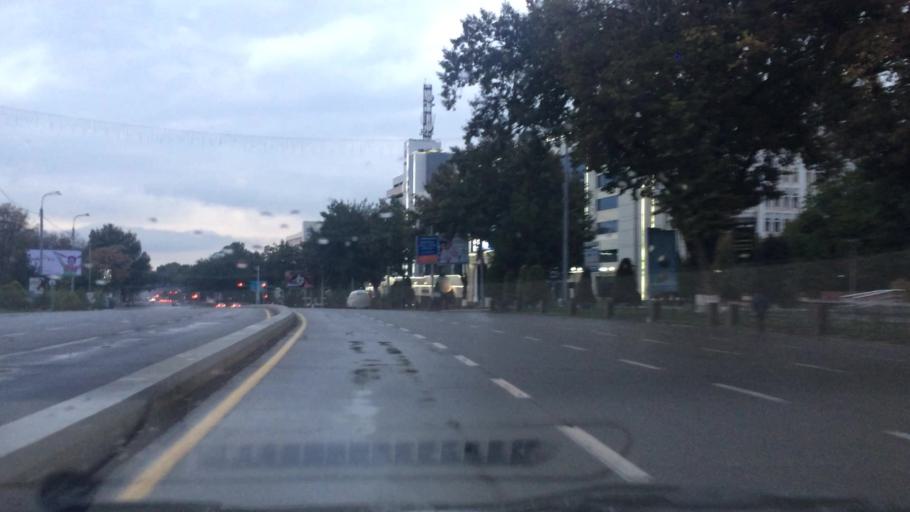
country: UZ
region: Toshkent Shahri
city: Tashkent
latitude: 41.3160
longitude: 69.2839
